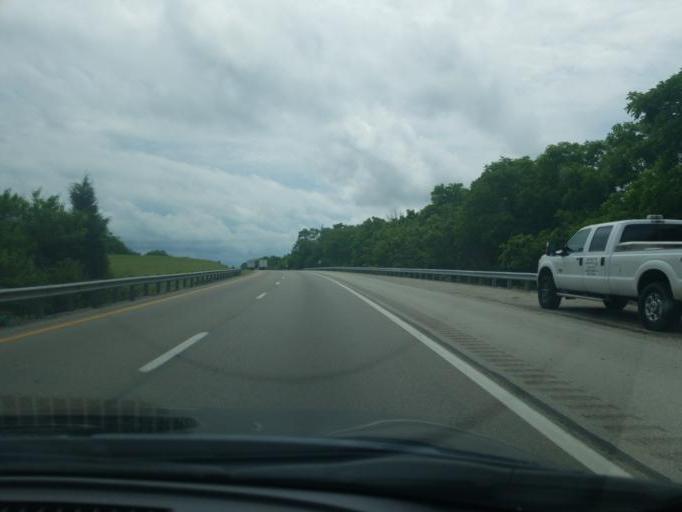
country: US
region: Indiana
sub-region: Switzerland County
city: Vevay
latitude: 38.6746
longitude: -85.0095
